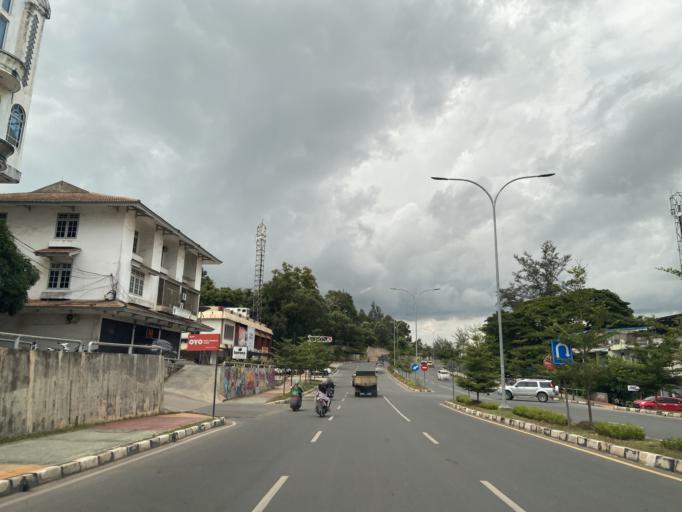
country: SG
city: Singapore
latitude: 1.1522
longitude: 104.0102
